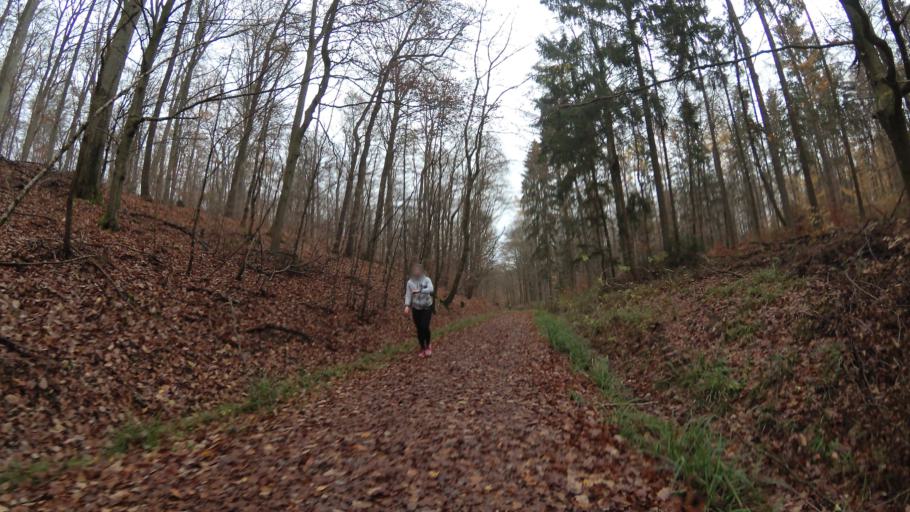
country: DE
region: Saarland
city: Friedrichsthal
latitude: 49.3507
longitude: 7.0881
